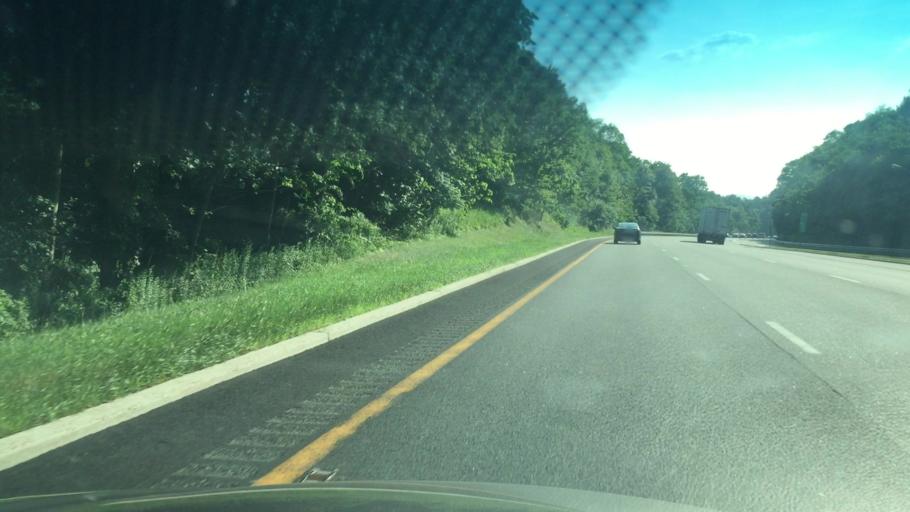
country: US
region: New Jersey
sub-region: Morris County
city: Budd Lake
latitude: 40.9245
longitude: -74.7928
